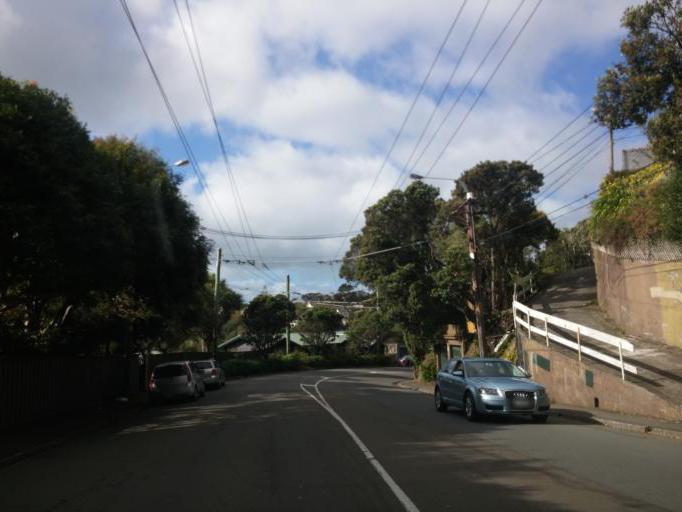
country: NZ
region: Wellington
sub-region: Wellington City
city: Kelburn
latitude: -41.2813
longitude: 174.7519
